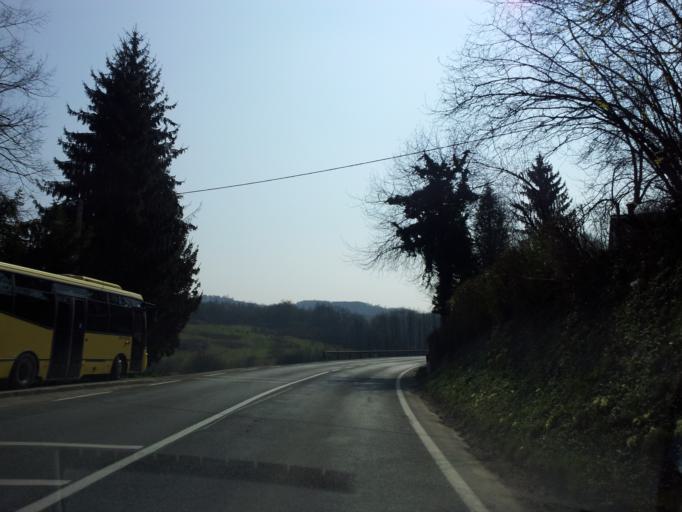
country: HR
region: Karlovacka
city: Vojnic
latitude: 45.3456
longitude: 15.6086
